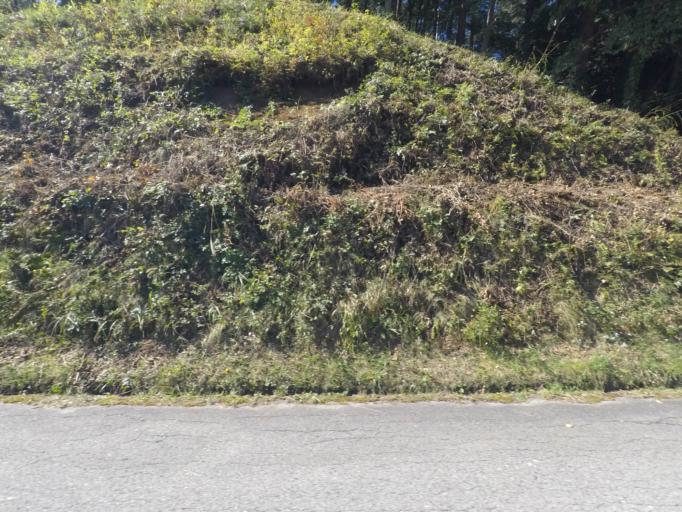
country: JP
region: Nagano
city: Ina
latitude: 35.9691
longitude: 137.7460
